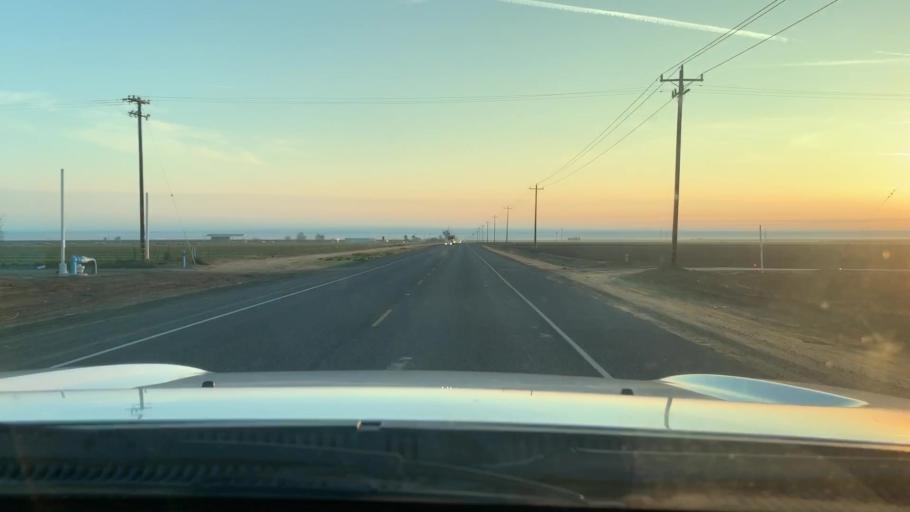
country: US
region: California
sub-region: Kern County
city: Lost Hills
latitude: 35.6011
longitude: -119.5542
